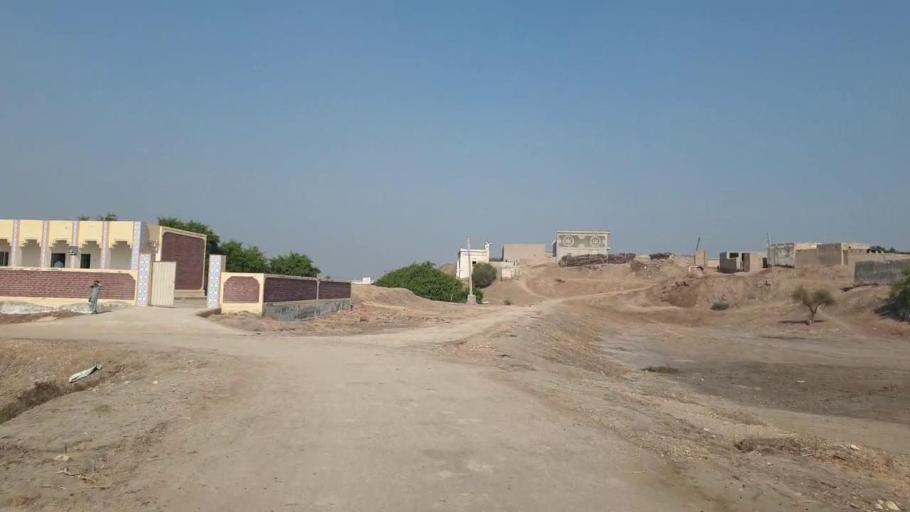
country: PK
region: Sindh
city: Sehwan
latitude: 26.4273
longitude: 67.7960
